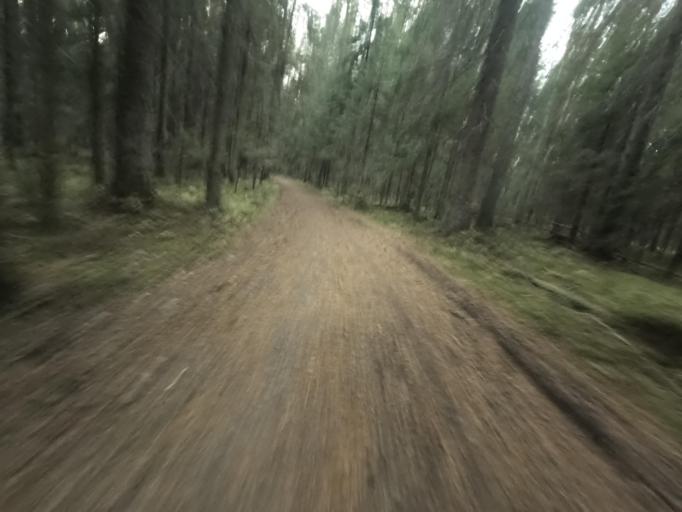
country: RU
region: Leningrad
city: Leninskoye
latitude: 60.1990
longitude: 29.8415
